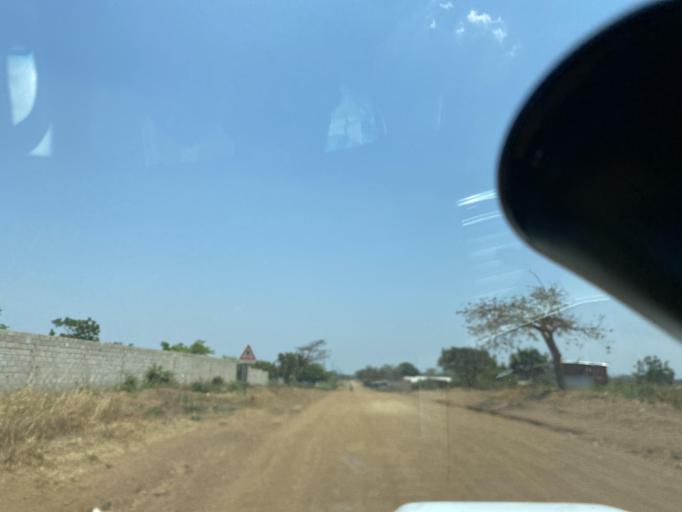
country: ZM
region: Lusaka
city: Lusaka
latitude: -15.4273
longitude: 28.0902
